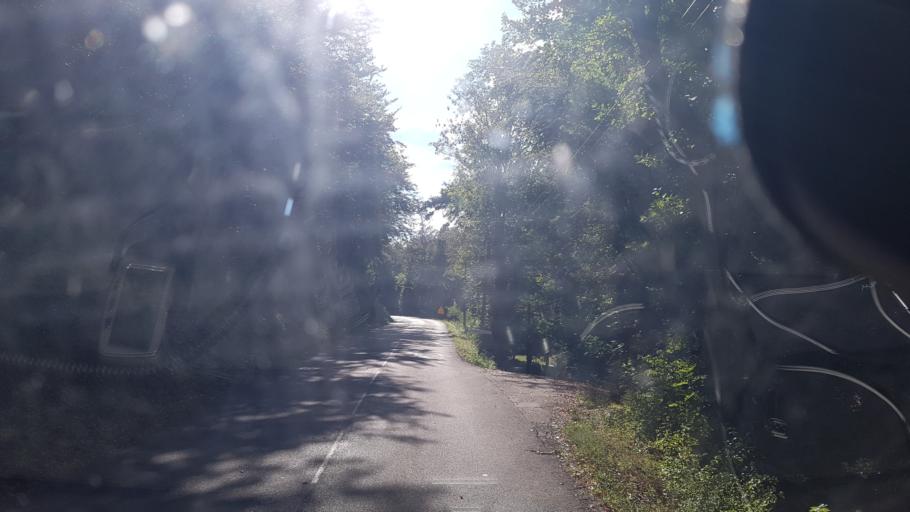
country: FR
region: Rhone-Alpes
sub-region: Departement de l'Isere
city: Mens
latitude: 44.8588
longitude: 5.6791
